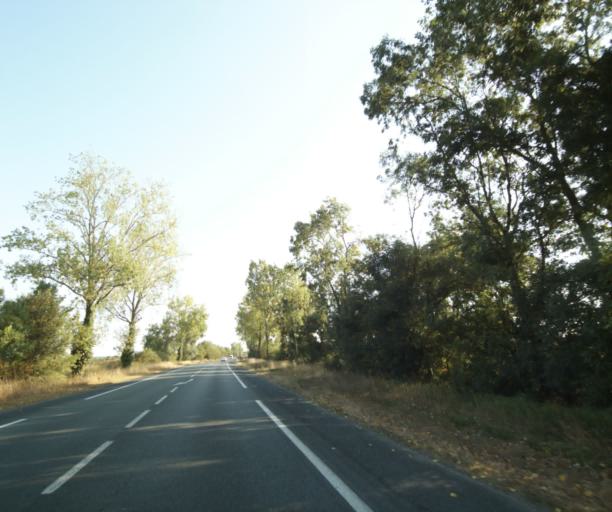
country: FR
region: Poitou-Charentes
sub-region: Departement de la Charente-Maritime
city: Saint-Hippolyte
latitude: 45.9220
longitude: -0.8838
